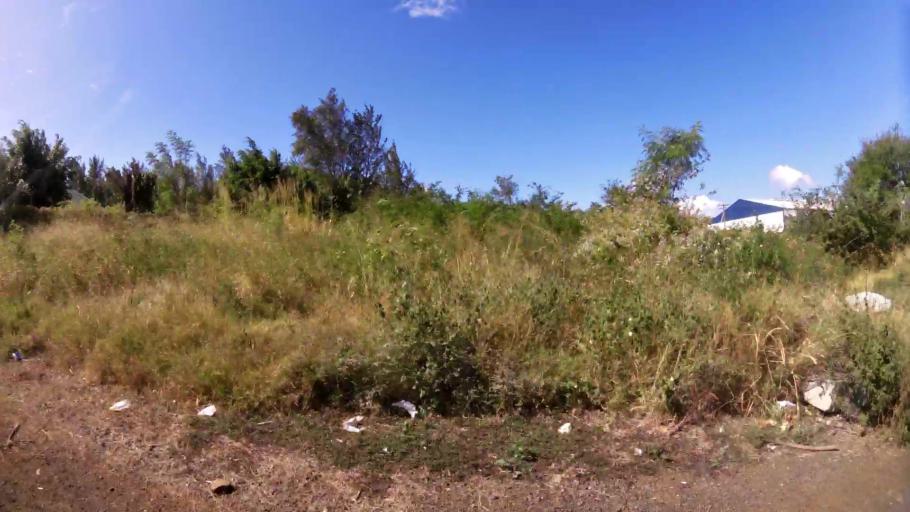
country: MU
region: Black River
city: Cascavelle
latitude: -20.2681
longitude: 57.4159
